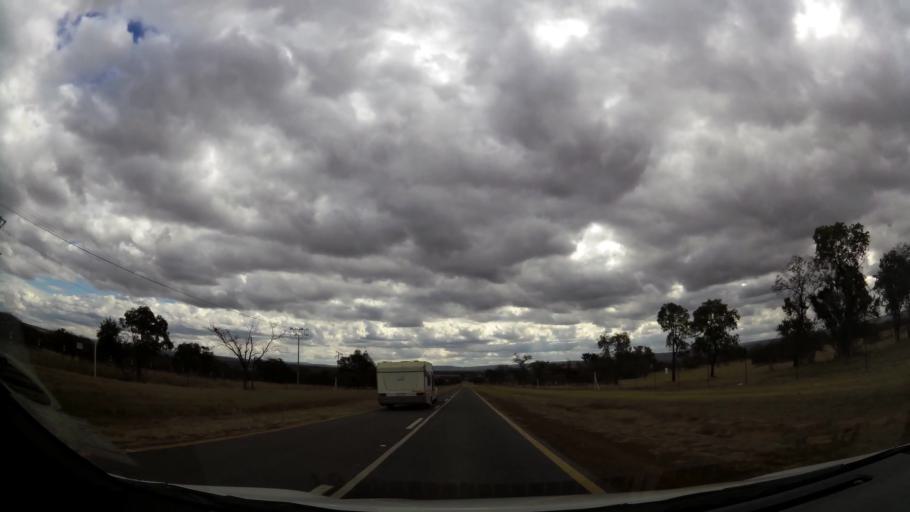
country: ZA
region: Limpopo
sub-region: Waterberg District Municipality
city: Modimolle
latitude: -24.7616
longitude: 28.4576
